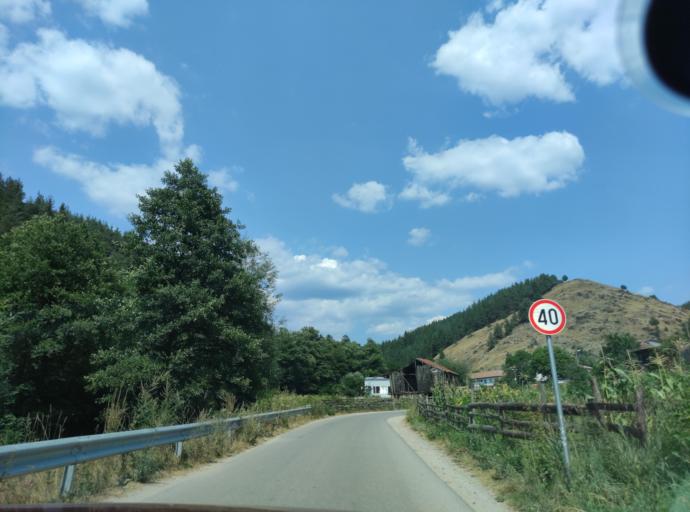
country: BG
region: Blagoevgrad
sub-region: Obshtina Belitsa
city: Belitsa
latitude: 41.9543
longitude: 23.5563
